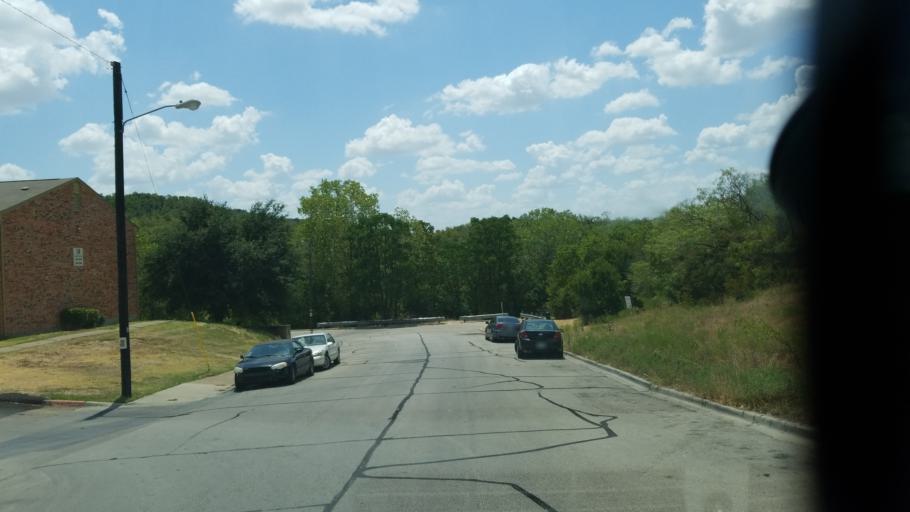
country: US
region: Texas
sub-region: Dallas County
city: Cockrell Hill
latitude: 32.7342
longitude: -96.9242
